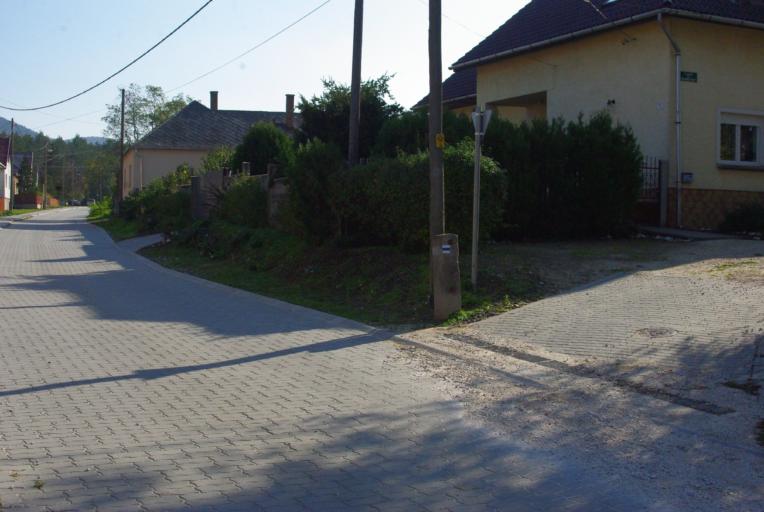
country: HU
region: Komarom-Esztergom
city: Piliscsev
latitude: 47.6714
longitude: 18.8182
